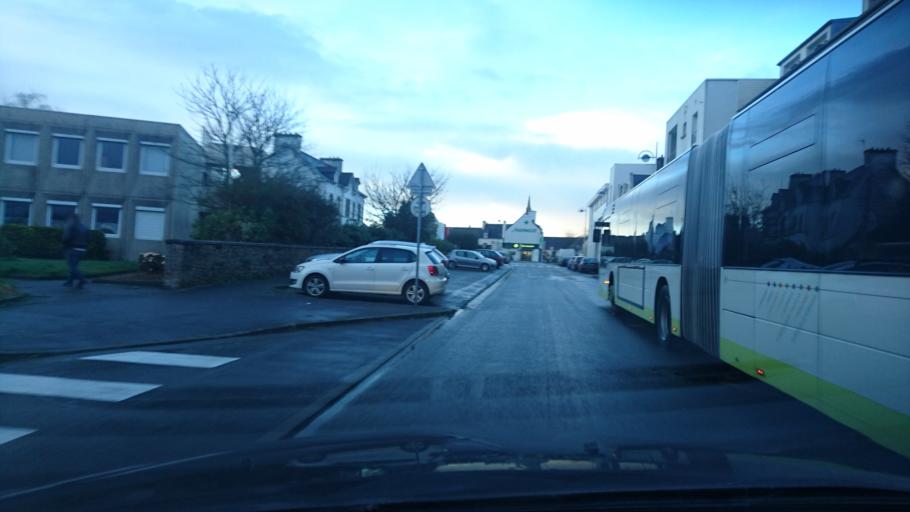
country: FR
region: Brittany
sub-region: Departement du Finistere
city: Guilers
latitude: 48.4234
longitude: -4.5587
